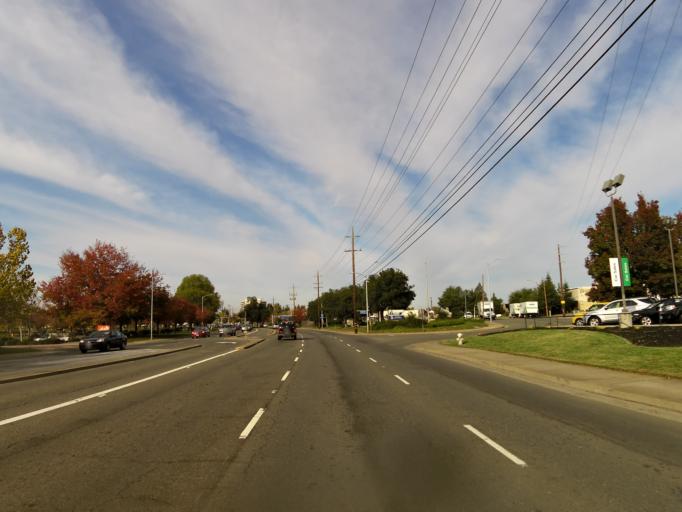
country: US
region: California
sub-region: Sacramento County
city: Gold River
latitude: 38.6008
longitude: -121.2660
